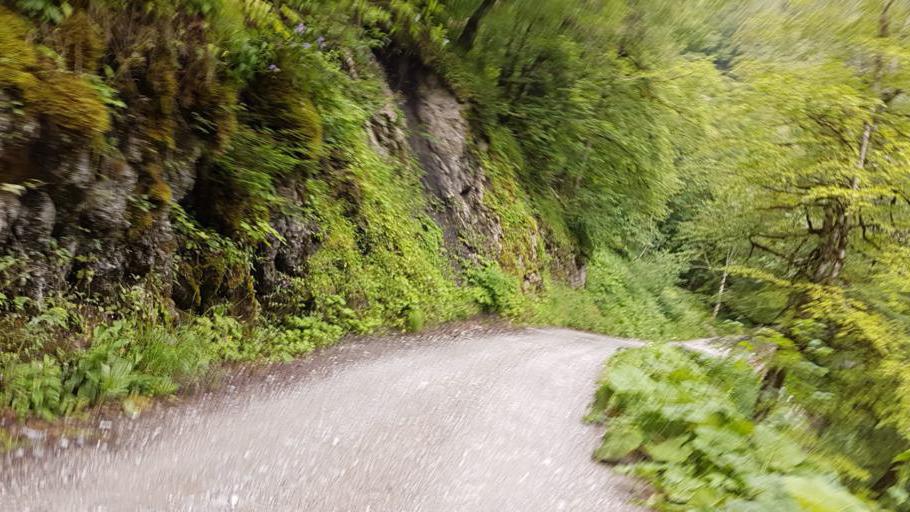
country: CH
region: Bern
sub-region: Obersimmental-Saanen District
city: Boltigen
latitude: 46.6734
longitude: 7.4570
